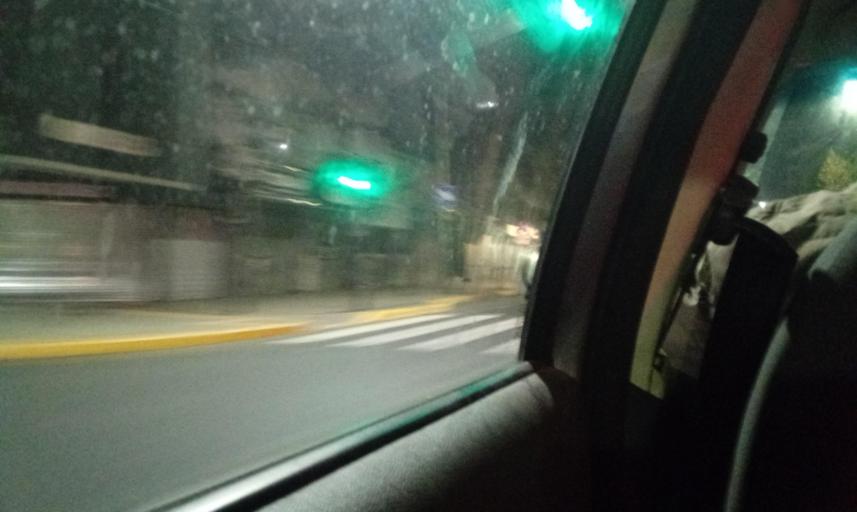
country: AR
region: Buenos Aires F.D.
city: Villa Santa Rita
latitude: -34.6269
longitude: -58.4732
